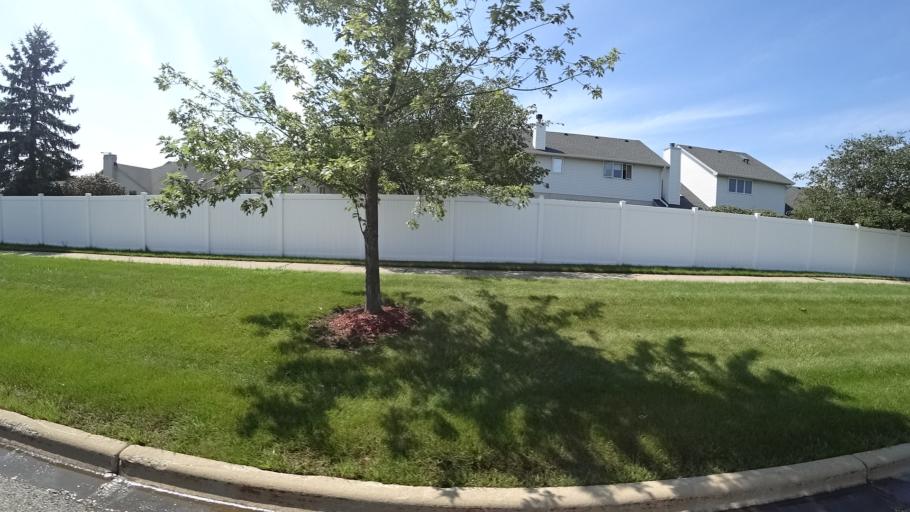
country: US
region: Illinois
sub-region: Cook County
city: Orland Hills
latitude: 41.5588
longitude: -87.8318
